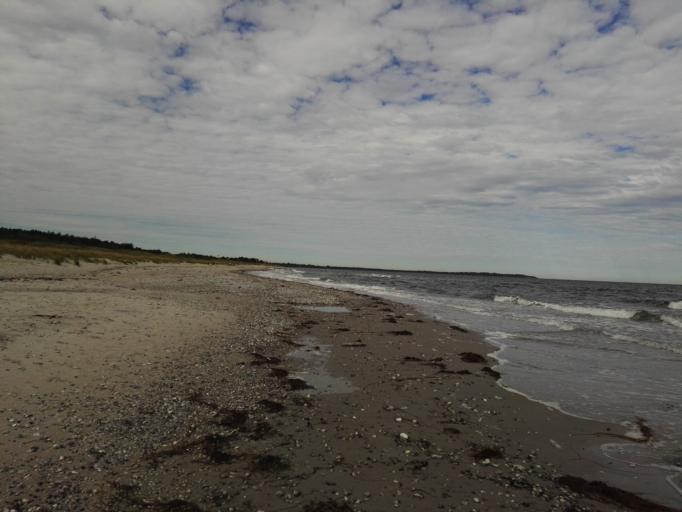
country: DK
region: Zealand
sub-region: Odsherred Kommune
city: Nykobing Sjaelland
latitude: 55.9468
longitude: 11.6925
